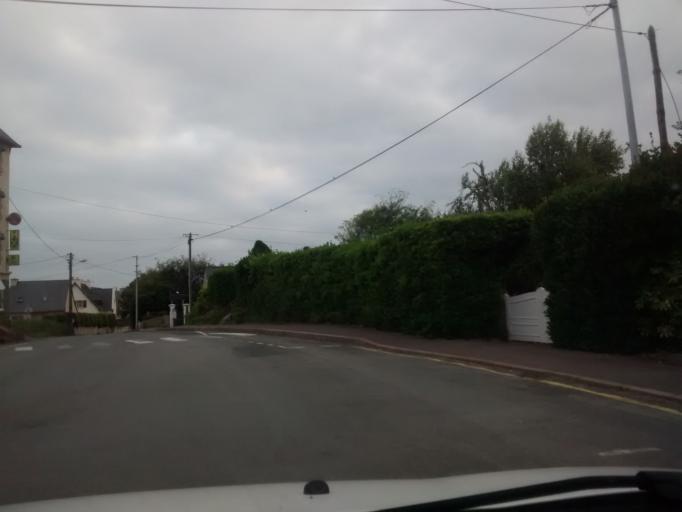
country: FR
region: Brittany
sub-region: Departement des Cotes-d'Armor
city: Tregastel
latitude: 48.8271
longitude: -3.4825
